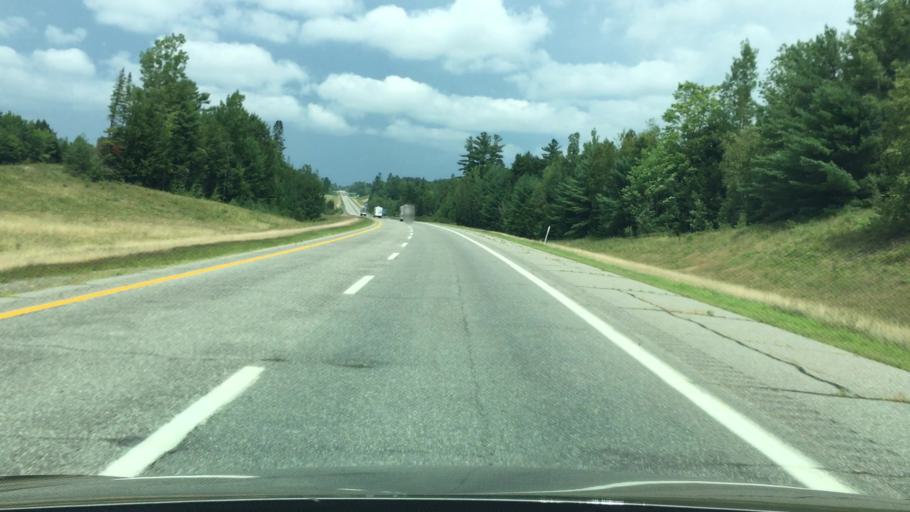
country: US
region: Maine
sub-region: Penobscot County
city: Lincoln
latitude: 45.3574
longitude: -68.6054
